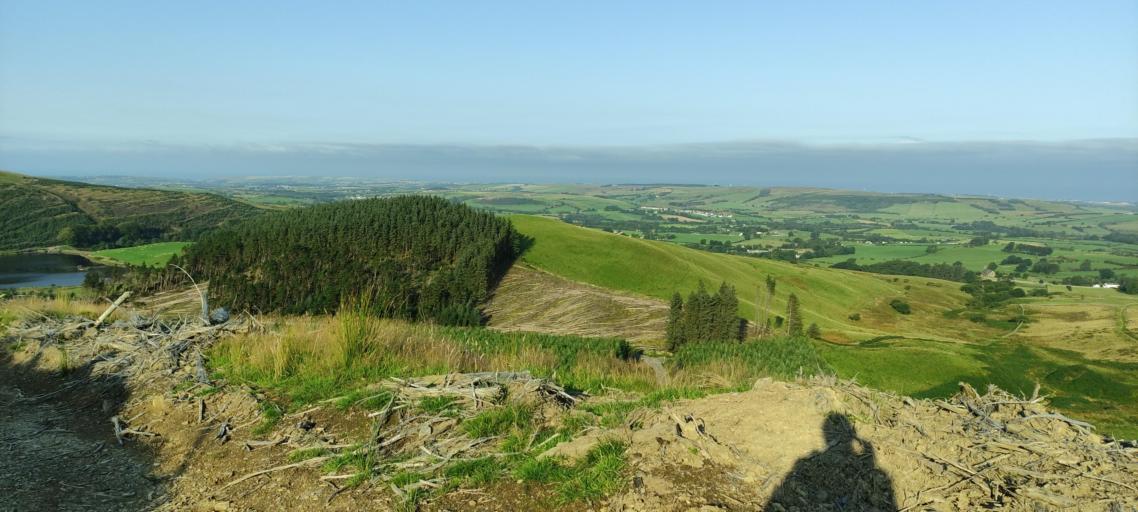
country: GB
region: England
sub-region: Cumbria
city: Cockermouth
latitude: 54.5702
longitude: -3.3902
